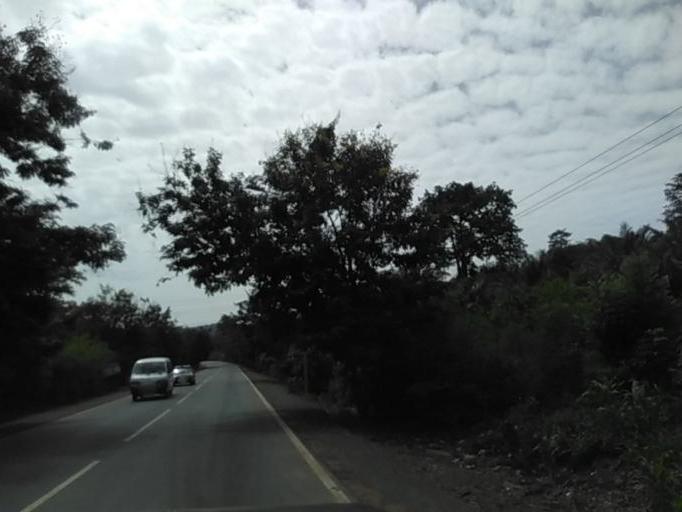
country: GH
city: Akropong
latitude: 6.2670
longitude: 0.0694
